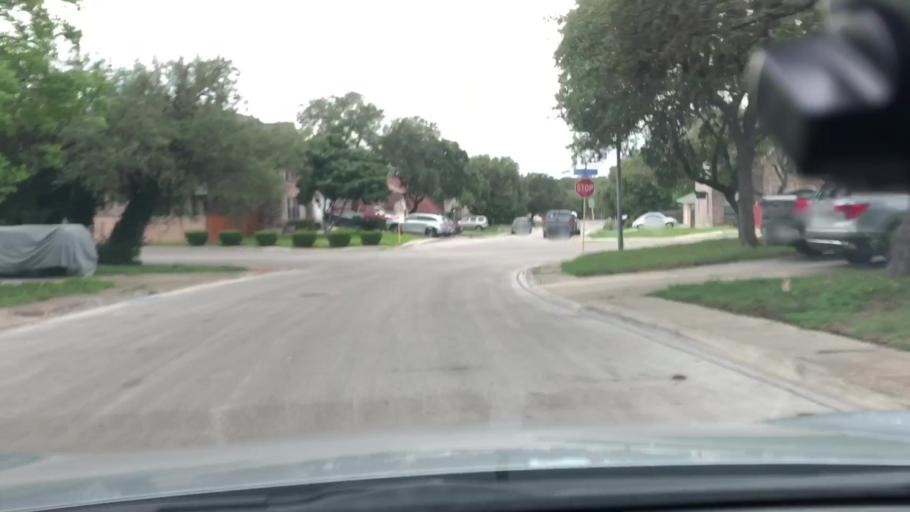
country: US
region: Texas
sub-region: Bexar County
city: Leon Valley
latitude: 29.5059
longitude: -98.6741
